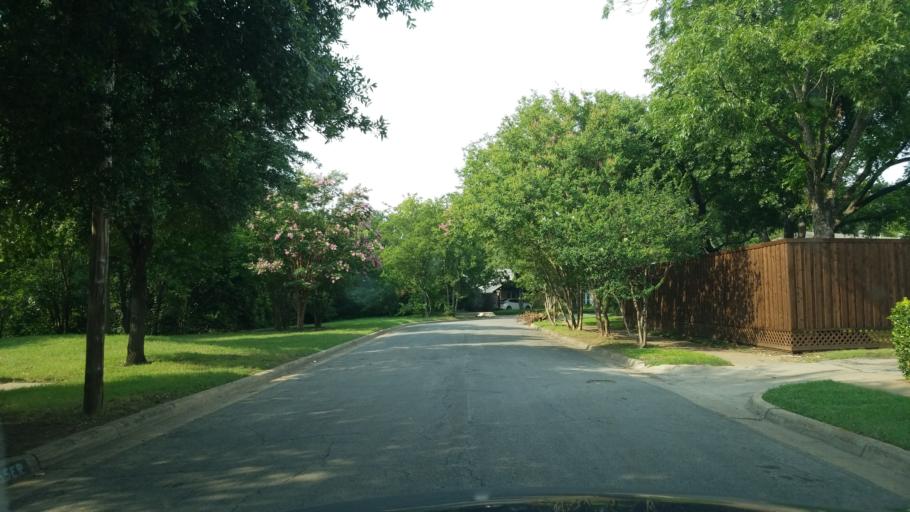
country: US
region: Texas
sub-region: Dallas County
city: Farmers Branch
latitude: 32.9106
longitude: -96.8457
